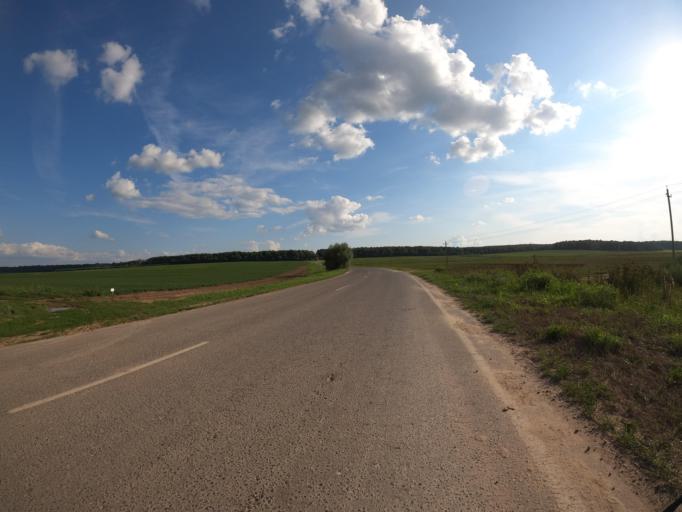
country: RU
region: Moskovskaya
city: Meshcherino
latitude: 55.1881
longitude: 38.4722
